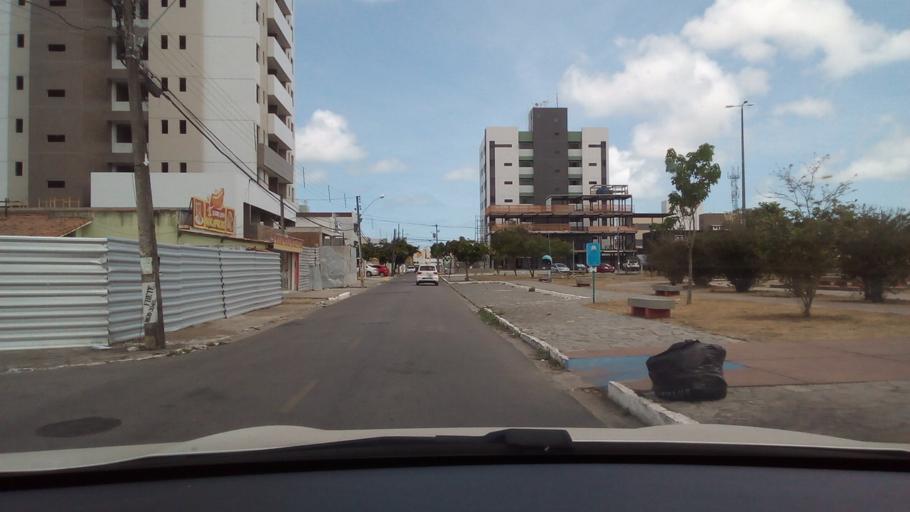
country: BR
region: Paraiba
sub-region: Joao Pessoa
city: Joao Pessoa
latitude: -7.1469
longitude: -34.8434
